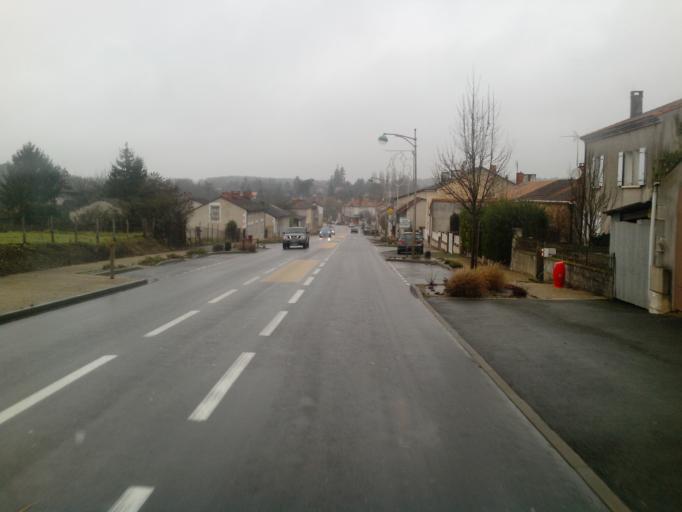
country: FR
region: Poitou-Charentes
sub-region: Departement de la Vienne
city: Terce
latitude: 46.4346
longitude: 0.6005
